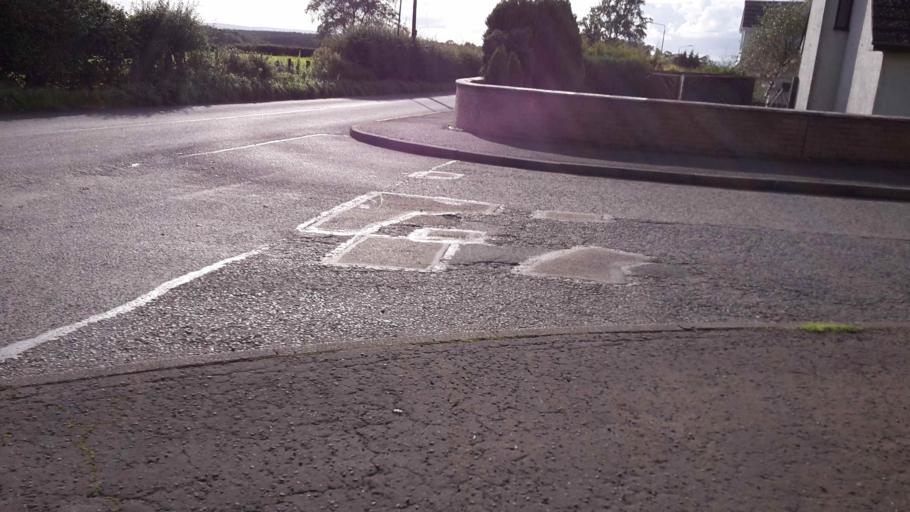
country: GB
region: Scotland
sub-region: South Lanarkshire
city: Carluke
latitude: 55.7243
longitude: -3.8286
